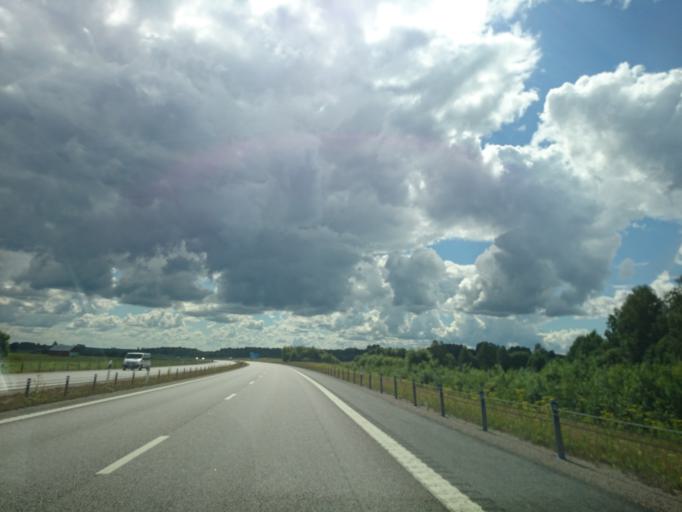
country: SE
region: Uppsala
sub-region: Tierps Kommun
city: Tierp
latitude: 60.3537
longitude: 17.4730
